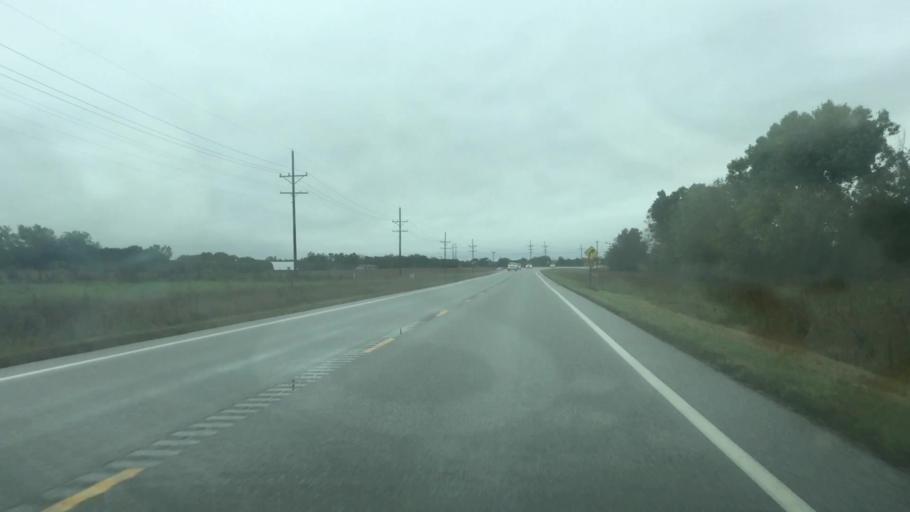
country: US
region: Kansas
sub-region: Anderson County
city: Garnett
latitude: 38.3407
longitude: -95.1645
